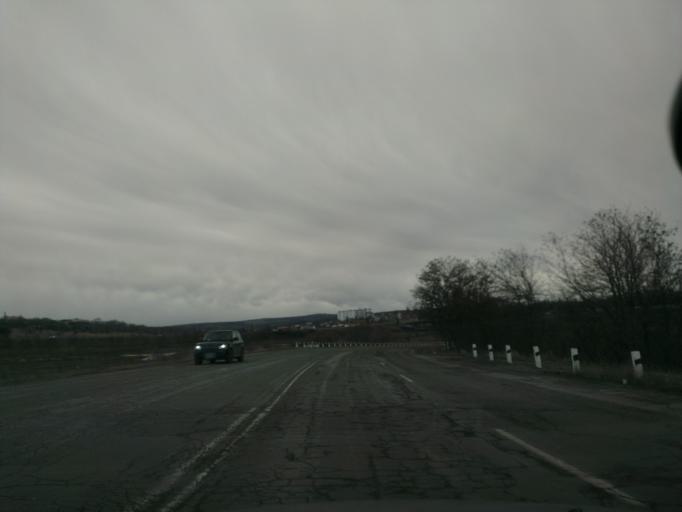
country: MD
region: Laloveni
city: Ialoveni
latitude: 46.9695
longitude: 28.7543
